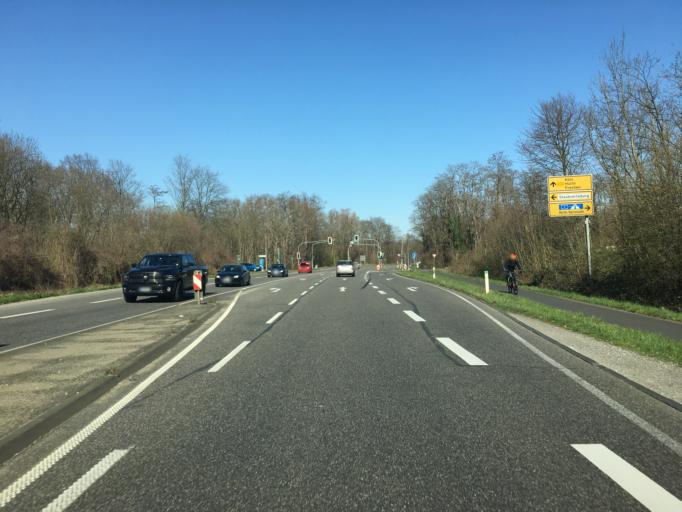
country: DE
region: North Rhine-Westphalia
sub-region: Regierungsbezirk Koln
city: Frechen
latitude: 50.8893
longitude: 6.7953
